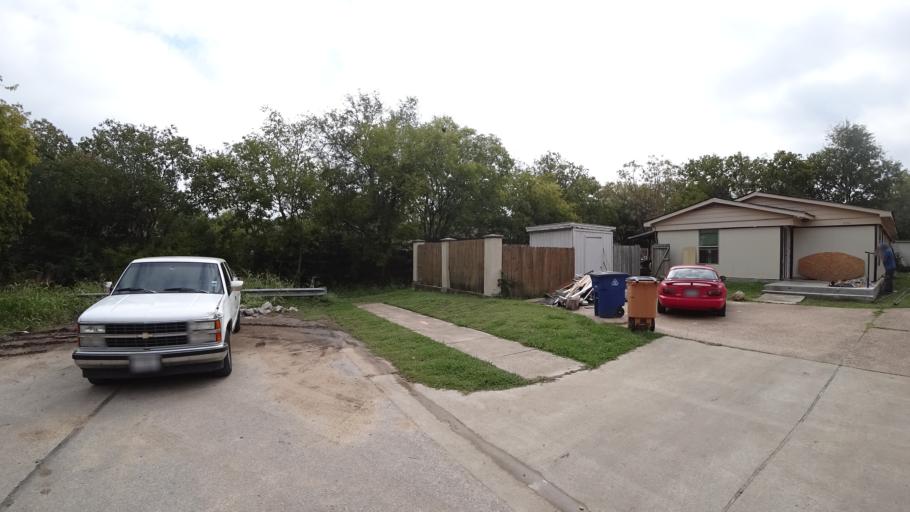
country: US
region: Texas
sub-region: Travis County
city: Shady Hollow
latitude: 30.2029
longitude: -97.8320
